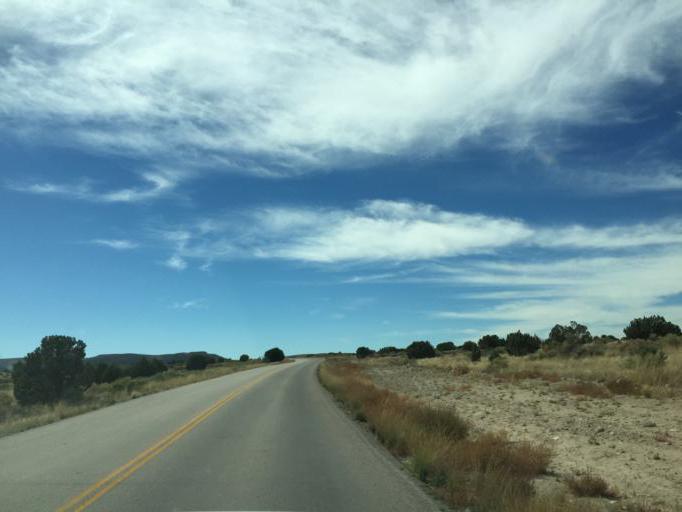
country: US
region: Arizona
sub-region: Mohave County
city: Meadview
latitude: 35.9569
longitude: -113.8420
